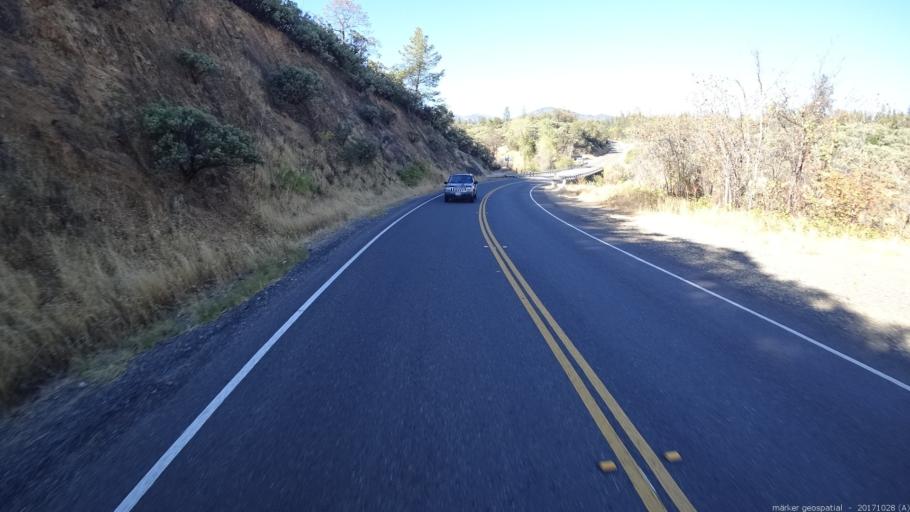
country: US
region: California
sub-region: Shasta County
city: Shasta
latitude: 40.6128
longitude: -122.4595
